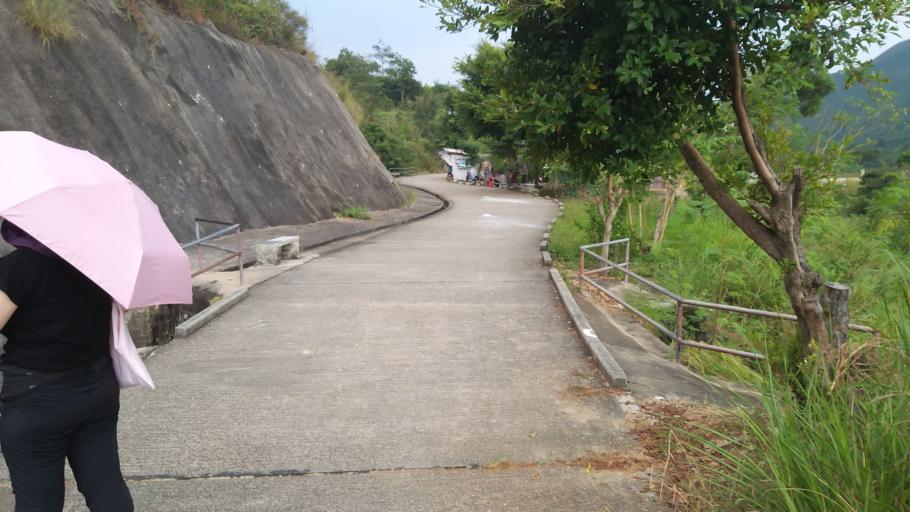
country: HK
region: Tuen Mun
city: Tuen Mun
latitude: 22.4079
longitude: 113.9529
